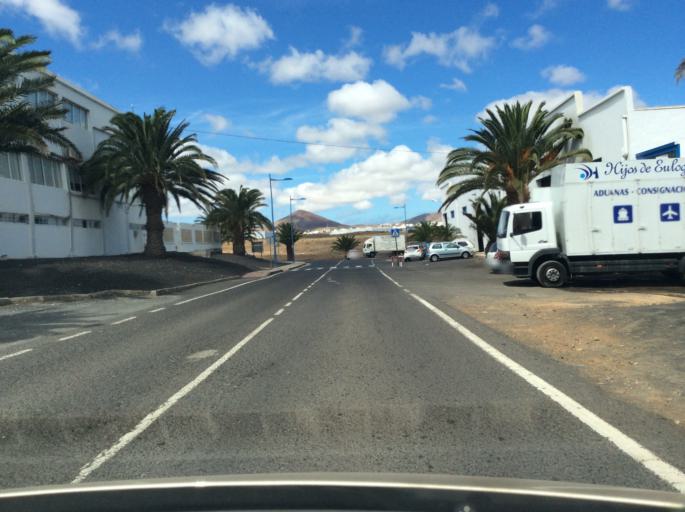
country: ES
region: Canary Islands
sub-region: Provincia de Las Palmas
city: Arrecife
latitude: 28.9743
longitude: -13.5331
